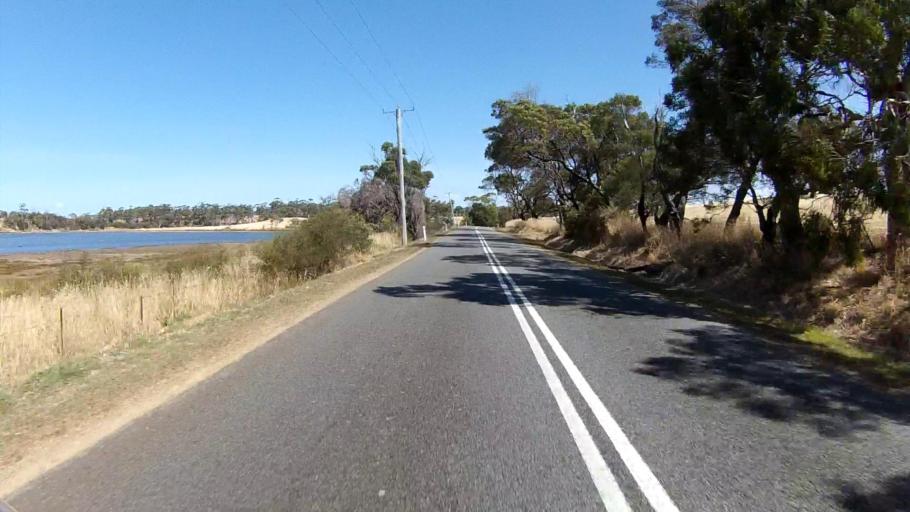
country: AU
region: Tasmania
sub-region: Sorell
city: Sorell
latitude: -42.2782
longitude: 148.0029
